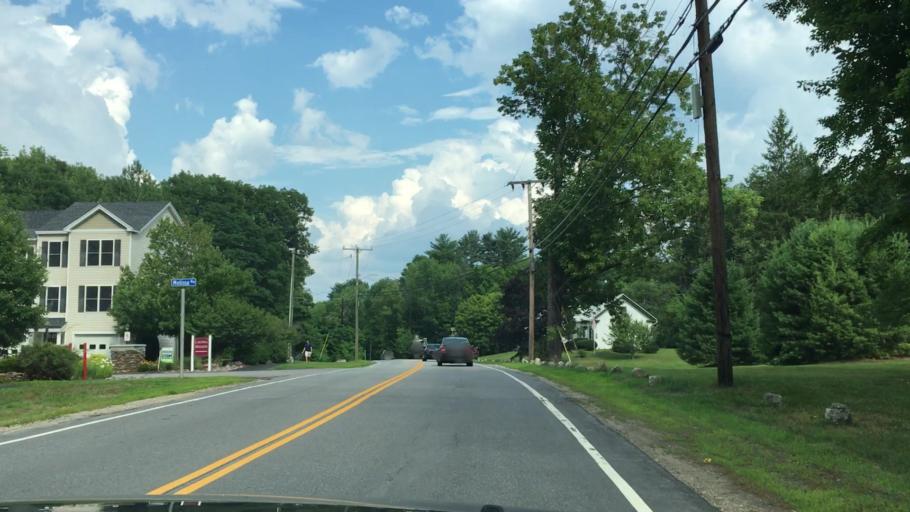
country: US
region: New Hampshire
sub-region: Belknap County
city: Gilford
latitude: 43.6020
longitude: -71.4476
